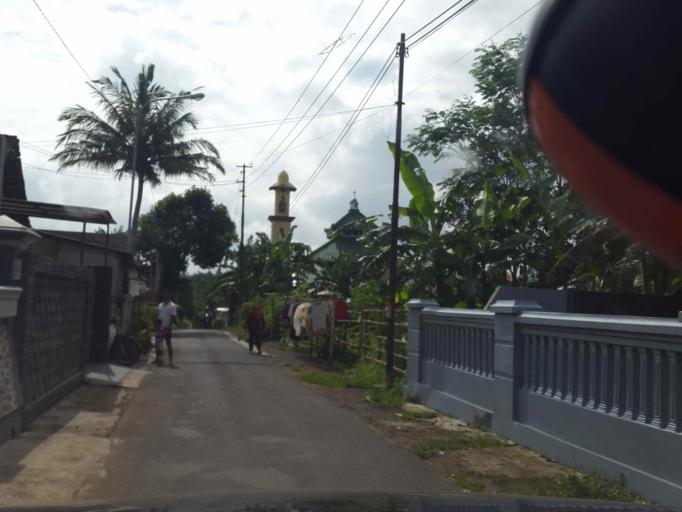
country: ID
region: Central Java
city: Salatiga
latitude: -7.3299
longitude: 110.5137
